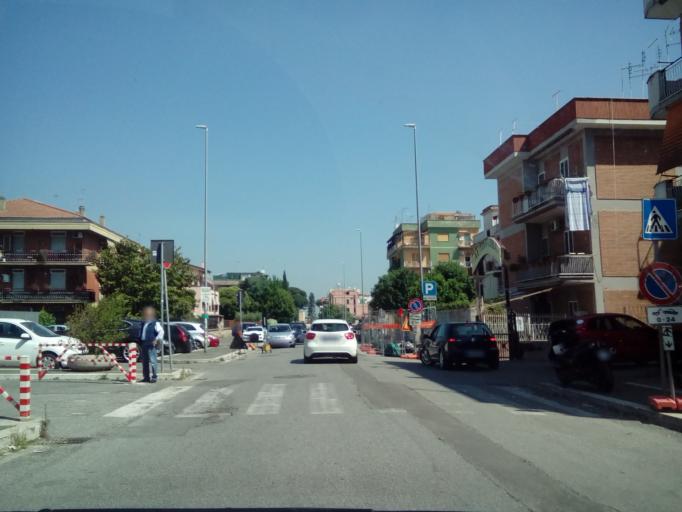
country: IT
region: Latium
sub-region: Citta metropolitana di Roma Capitale
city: Rome
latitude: 41.8832
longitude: 12.5771
